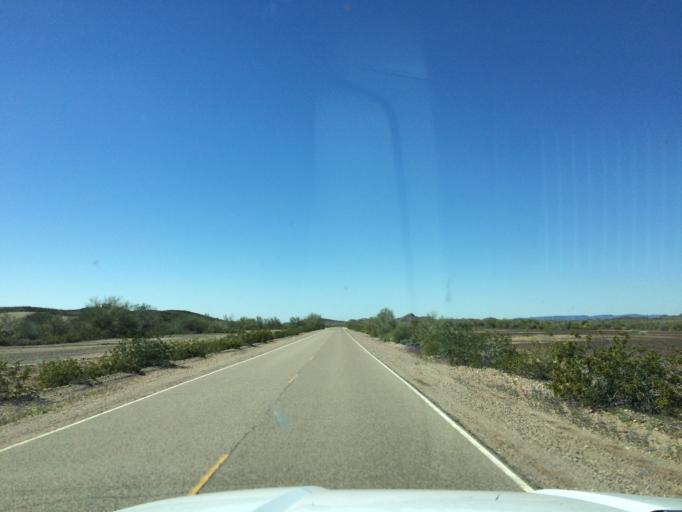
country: US
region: Arizona
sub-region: Yuma County
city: Wellton
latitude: 32.9696
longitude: -114.2841
